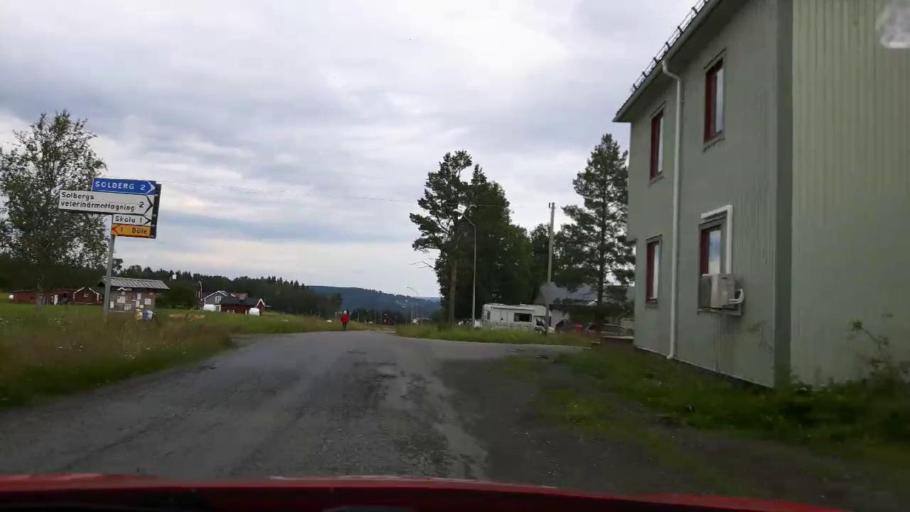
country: SE
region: Jaemtland
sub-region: Stroemsunds Kommun
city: Stroemsund
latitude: 63.5229
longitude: 15.3547
